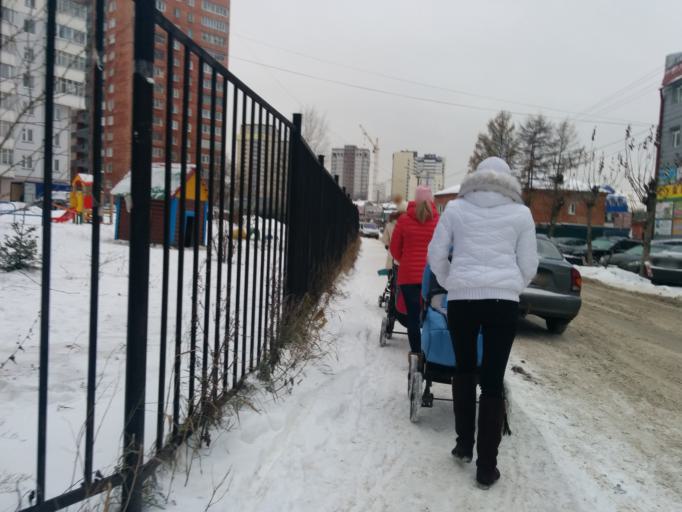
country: RU
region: Perm
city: Perm
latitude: 57.9970
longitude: 56.2053
